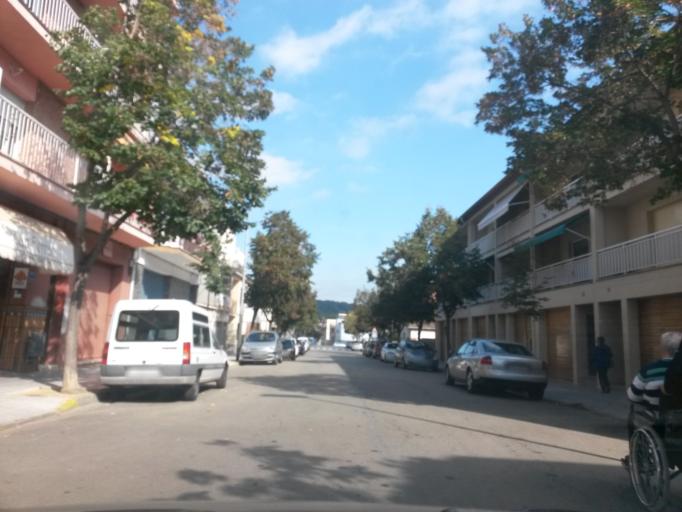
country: ES
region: Catalonia
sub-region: Provincia de Girona
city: Bescano
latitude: 41.9648
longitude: 2.7386
